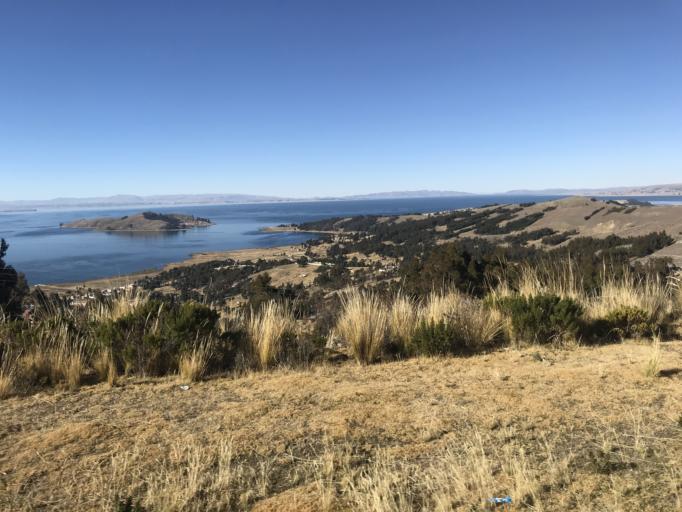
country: BO
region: La Paz
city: San Pedro
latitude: -16.1883
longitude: -68.9686
